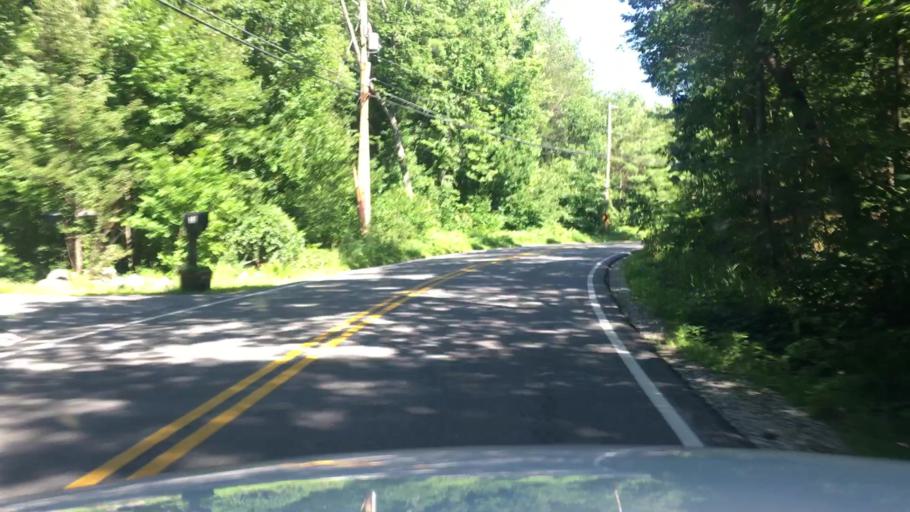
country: US
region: New Hampshire
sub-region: Merrimack County
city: South Hooksett
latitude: 43.0396
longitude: -71.4064
